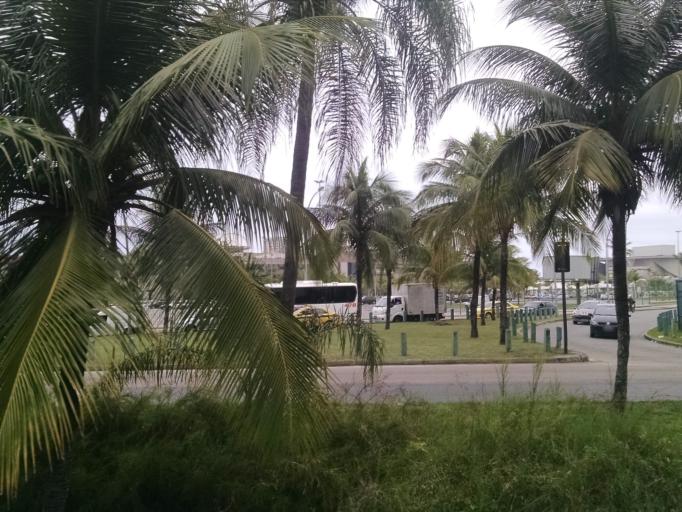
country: BR
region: Rio de Janeiro
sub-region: Rio De Janeiro
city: Rio de Janeiro
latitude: -22.9948
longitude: -43.3591
